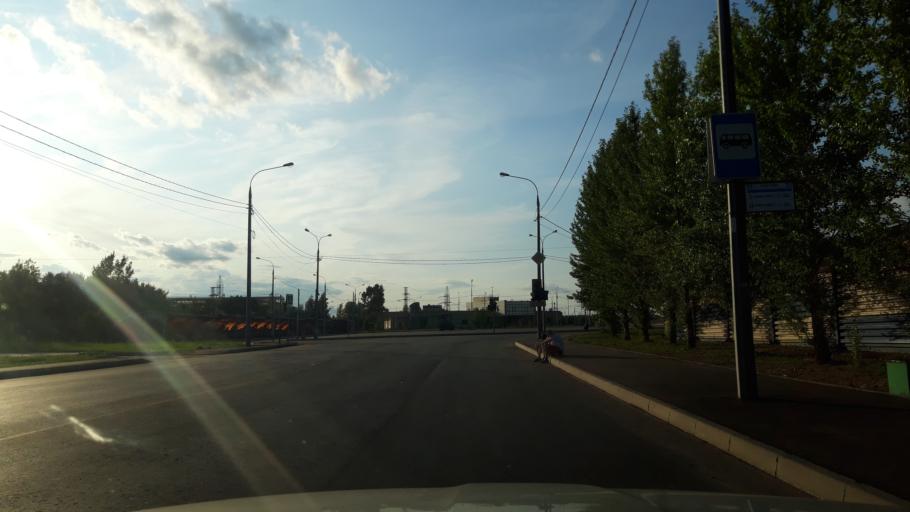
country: RU
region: Moskovskaya
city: Alabushevo
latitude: 56.0078
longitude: 37.1427
